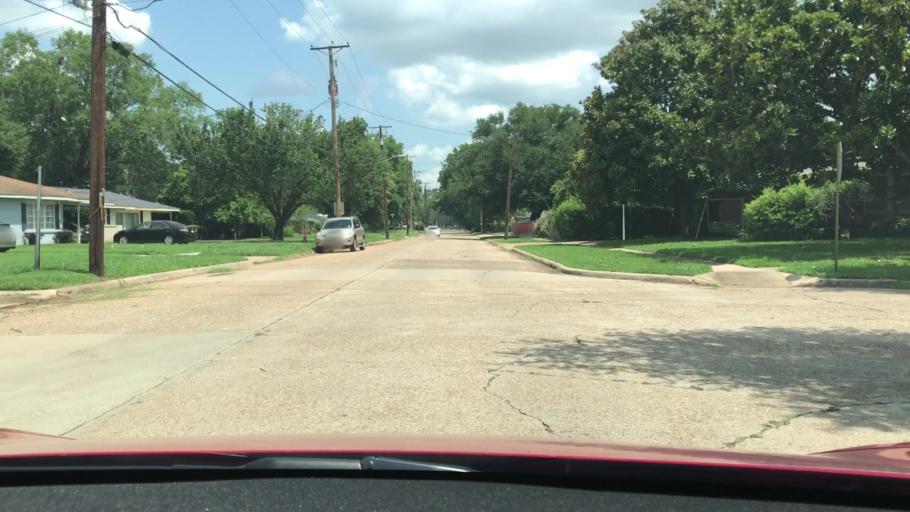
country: US
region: Louisiana
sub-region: Bossier Parish
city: Bossier City
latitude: 32.4575
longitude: -93.7282
